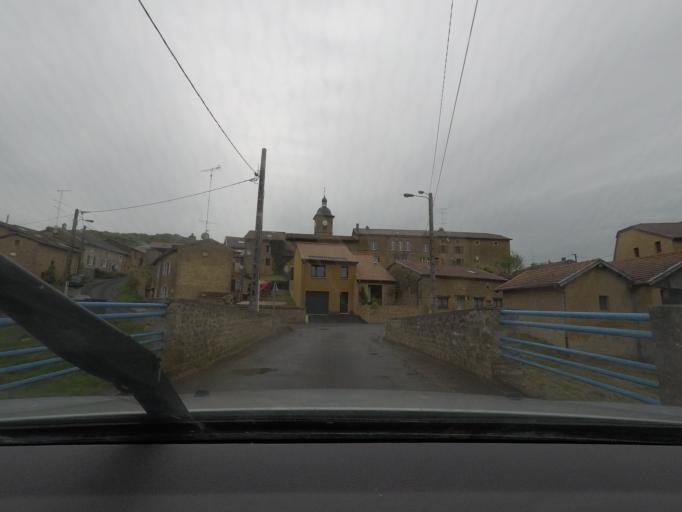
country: FR
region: Lorraine
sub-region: Departement de la Meuse
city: Montmedy
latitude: 49.4964
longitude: 5.4291
